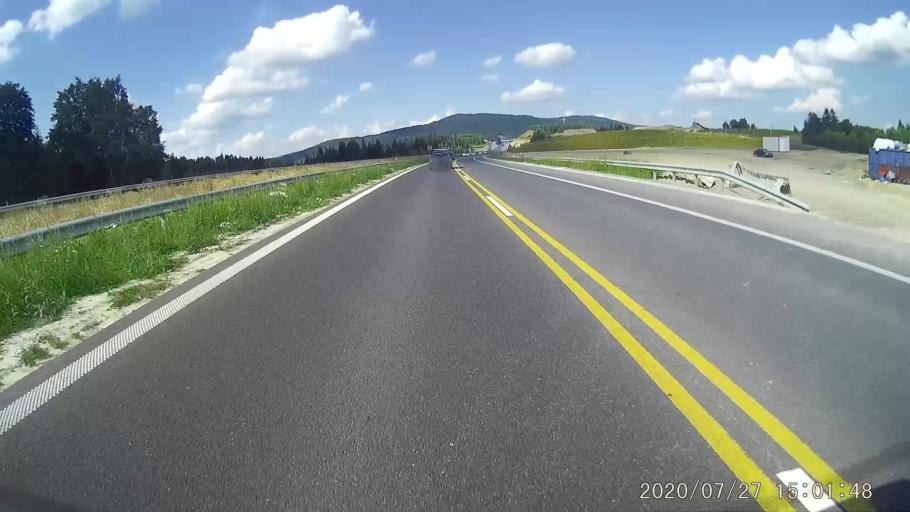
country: PL
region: Lesser Poland Voivodeship
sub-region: Powiat suski
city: Letownia
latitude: 49.6786
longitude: 19.8889
